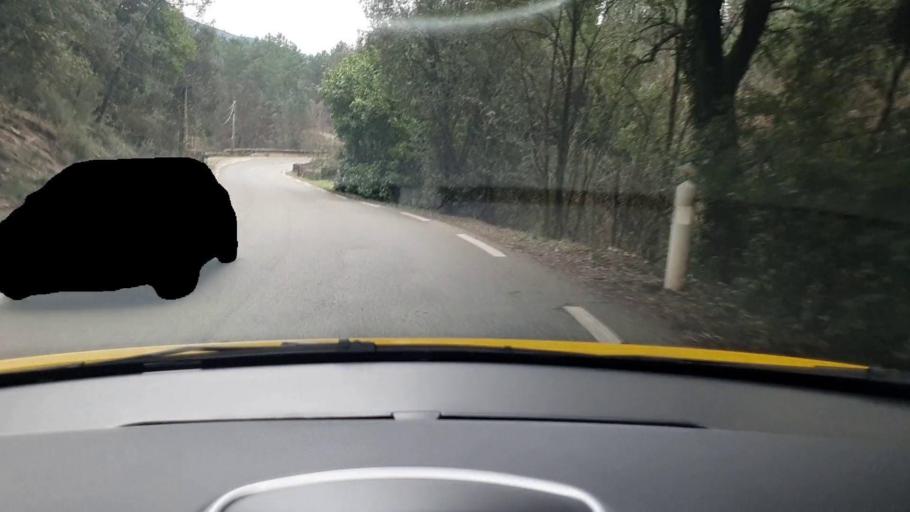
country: FR
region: Languedoc-Roussillon
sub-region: Departement du Gard
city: Les Salles-du-Gardon
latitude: 44.2517
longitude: 4.0463
